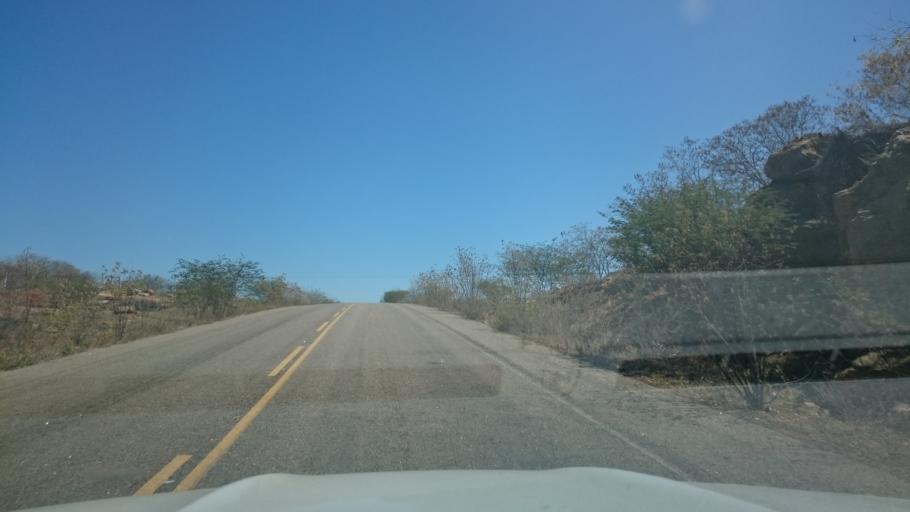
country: BR
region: Paraiba
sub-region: Catole Do Rocha
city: Sao Bento
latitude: -6.2034
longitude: -37.9456
